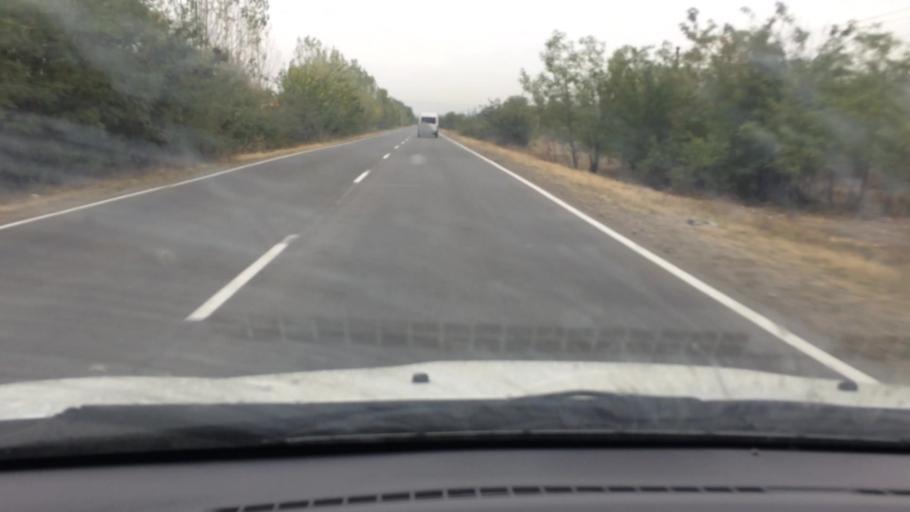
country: GE
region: Kvemo Kartli
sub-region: Marneuli
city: Marneuli
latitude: 41.4460
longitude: 44.8154
